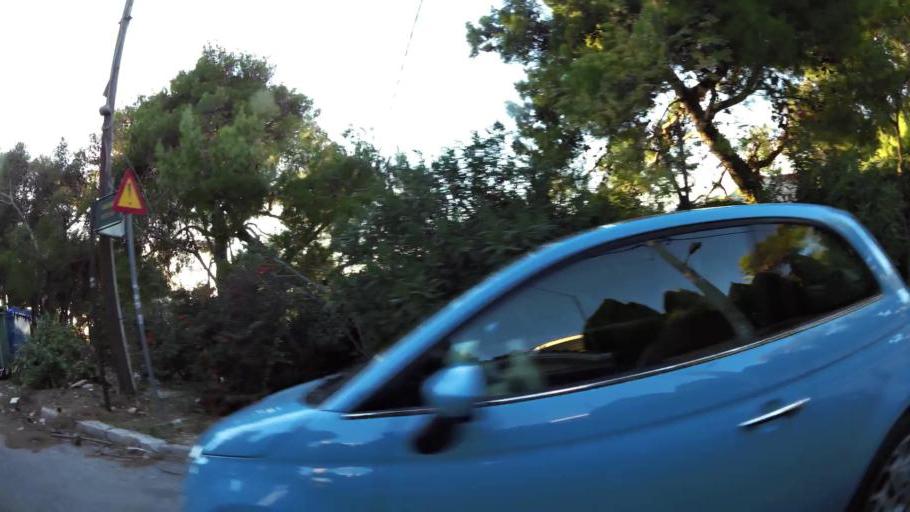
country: GR
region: Attica
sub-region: Nomarchia Athinas
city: Penteli
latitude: 38.0492
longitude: 23.8605
